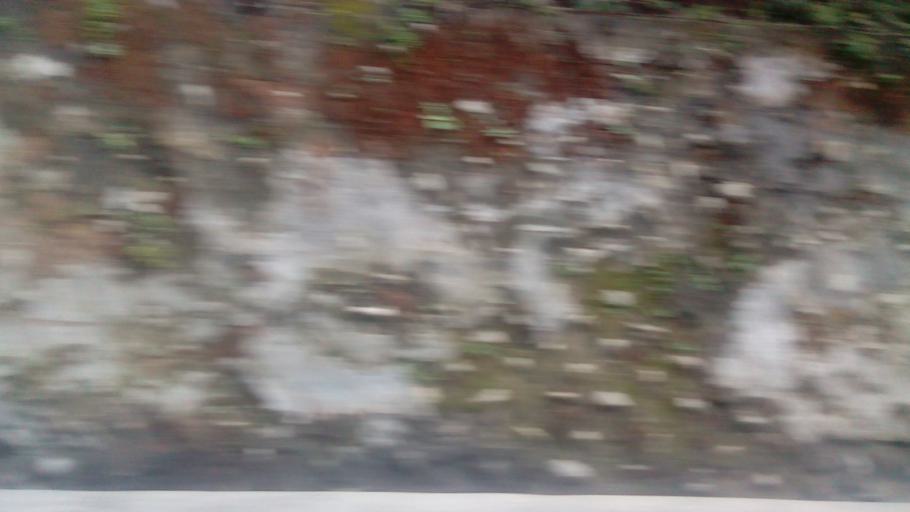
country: TW
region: Taiwan
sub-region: Yilan
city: Yilan
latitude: 24.5707
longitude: 121.4732
